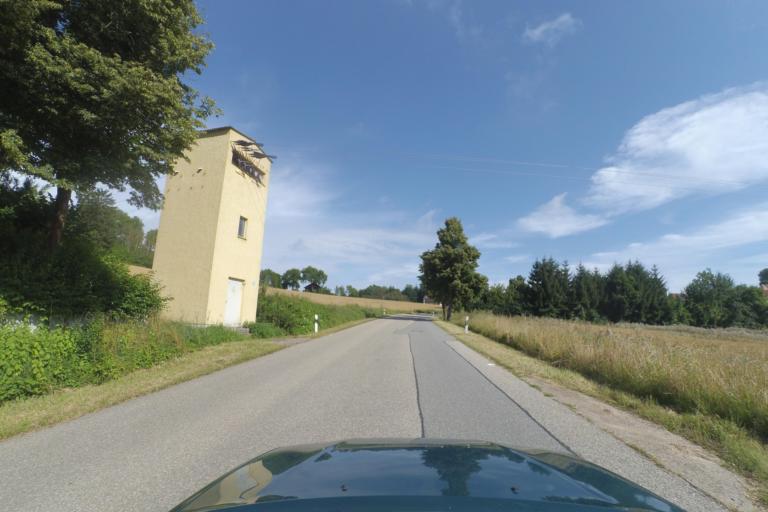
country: DE
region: Bavaria
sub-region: Lower Bavaria
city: Teugn
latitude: 48.9332
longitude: 11.9859
